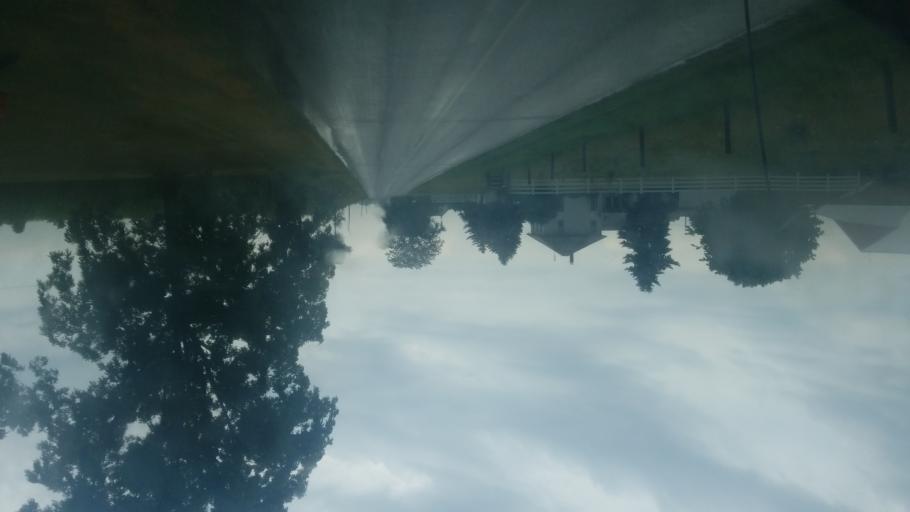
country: US
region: Indiana
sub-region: DeKalb County
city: Butler
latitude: 41.4731
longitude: -84.8541
